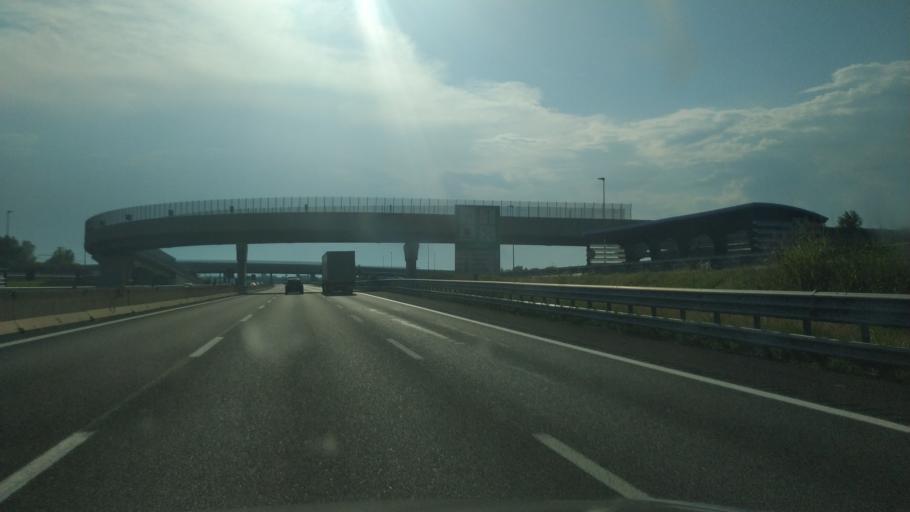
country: IT
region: Piedmont
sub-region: Provincia di Vercelli
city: Greggio
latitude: 45.4621
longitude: 8.3805
